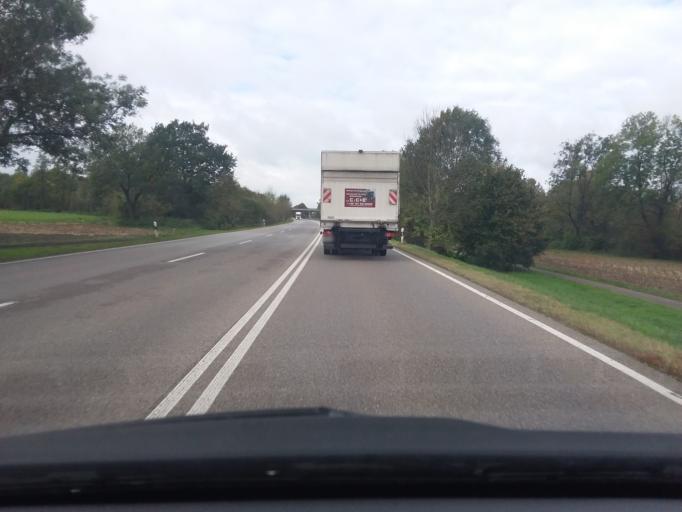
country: DE
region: Bavaria
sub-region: Upper Bavaria
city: Bergkirchen
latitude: 48.2400
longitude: 11.3809
